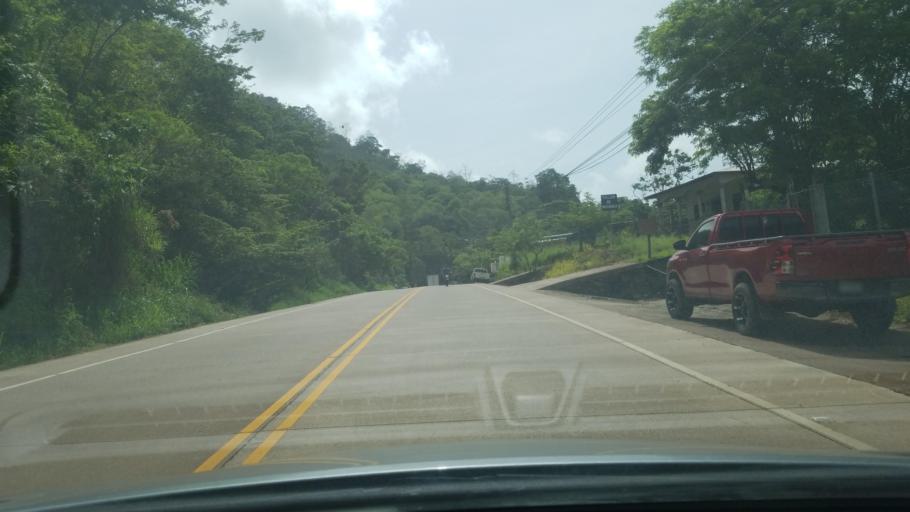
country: HN
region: Copan
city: Buenos Aires
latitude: 14.9285
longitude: -88.9720
